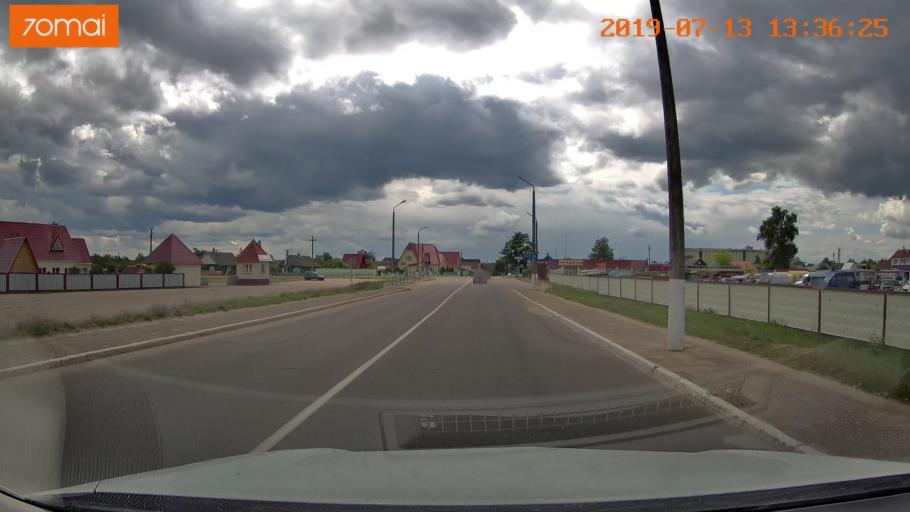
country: BY
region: Mogilev
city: Asipovichy
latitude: 53.3023
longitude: 28.6224
